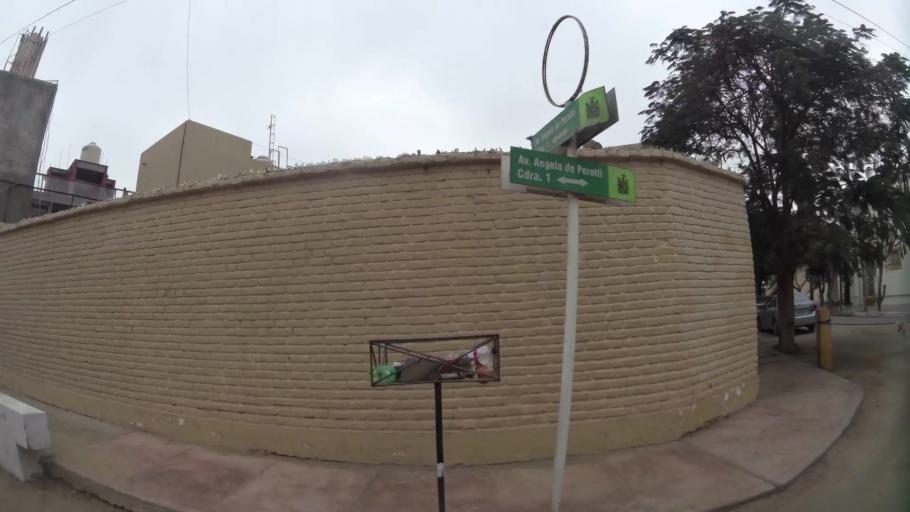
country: PE
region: Ica
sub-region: Provincia de Ica
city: Ica
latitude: -14.0868
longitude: -75.7648
